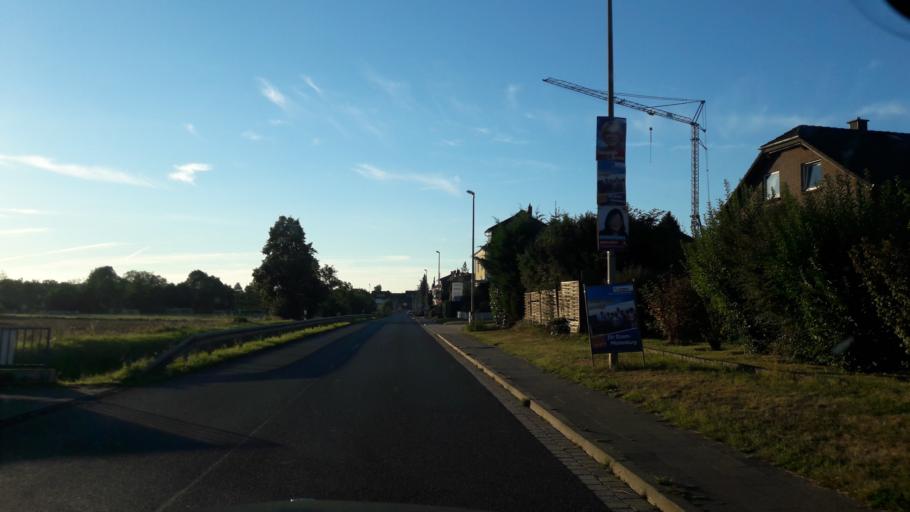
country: DE
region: Lower Saxony
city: Hildesheim
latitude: 52.1144
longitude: 9.9884
